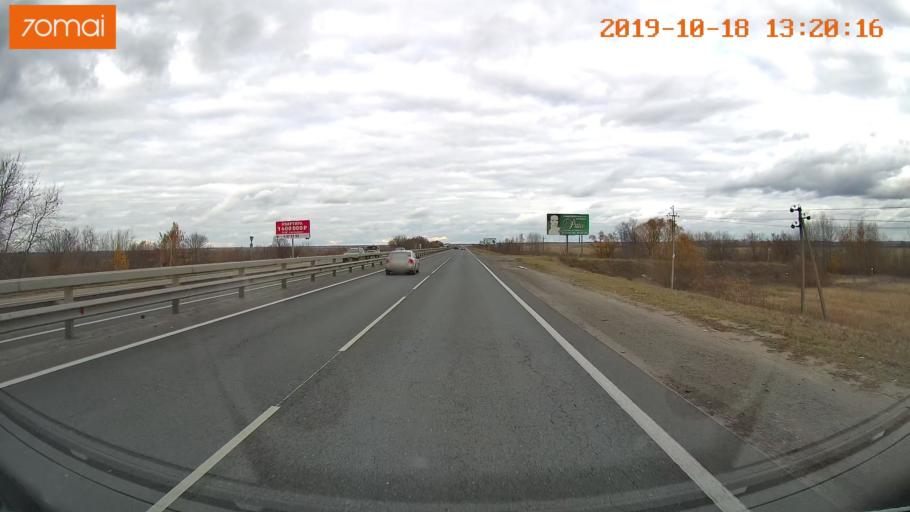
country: RU
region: Rjazan
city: Polyany
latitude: 54.6779
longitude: 39.8303
